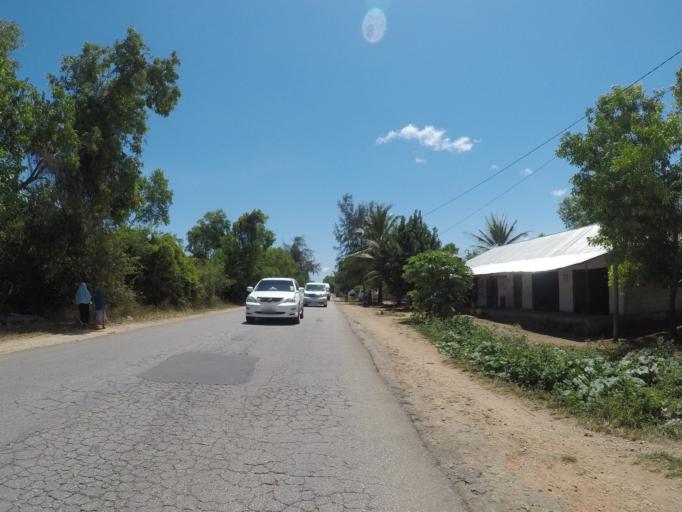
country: TZ
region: Zanzibar Central/South
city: Mahonda
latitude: -6.2838
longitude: 39.4088
